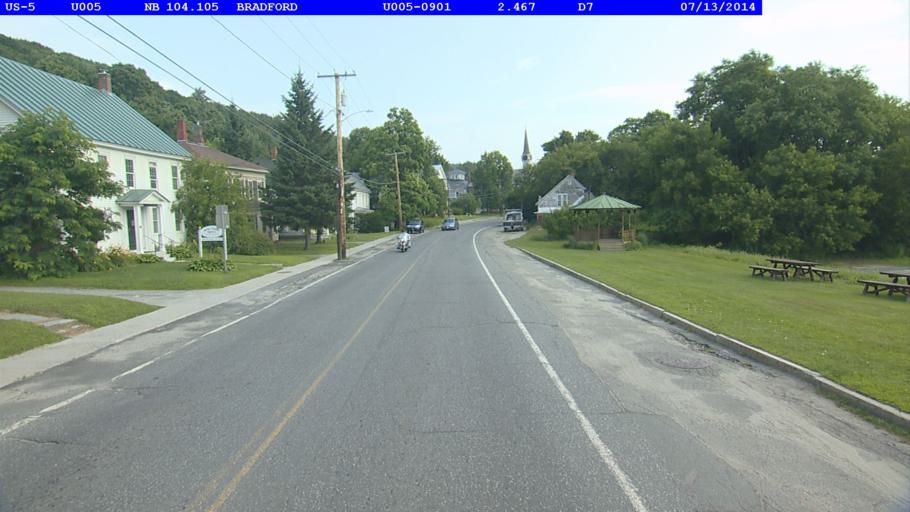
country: US
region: New Hampshire
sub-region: Grafton County
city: Haverhill
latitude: 43.9954
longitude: -72.1280
